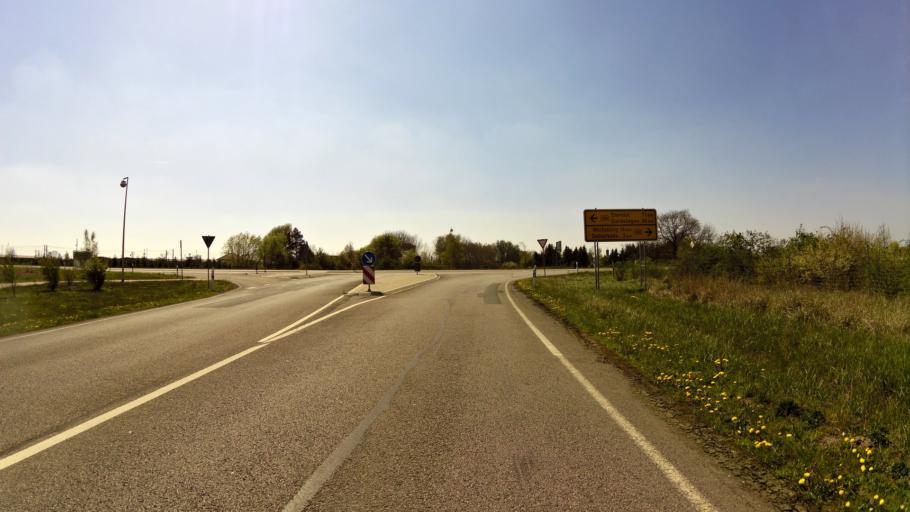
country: DE
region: Saxony-Anhalt
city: Oebisfelde
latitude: 52.4440
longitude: 10.9950
